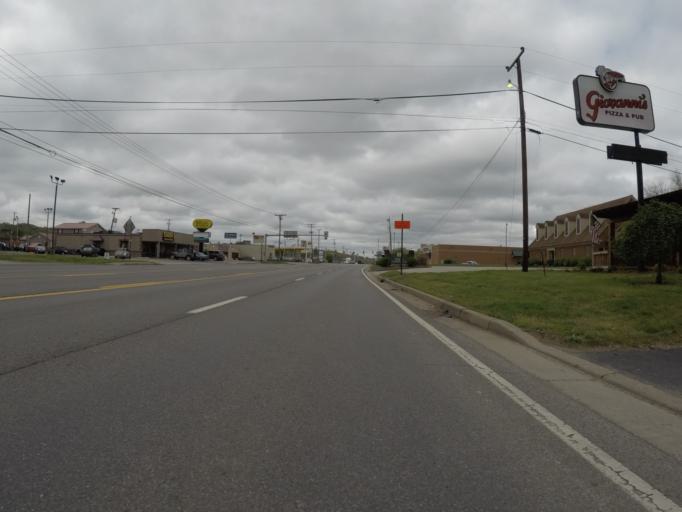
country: US
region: West Virginia
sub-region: Cabell County
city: Barboursville
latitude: 38.4155
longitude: -82.2975
